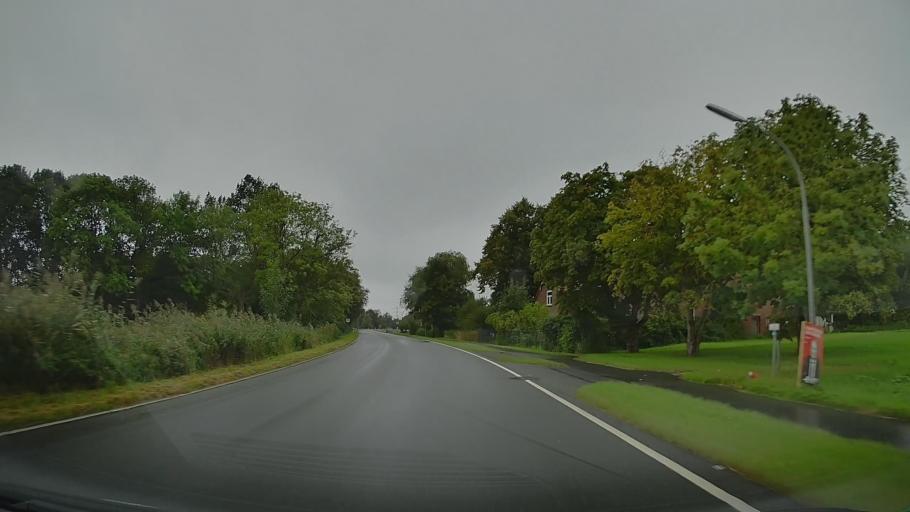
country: DE
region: Schleswig-Holstein
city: Sankt Margarethen
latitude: 53.8949
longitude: 9.2458
